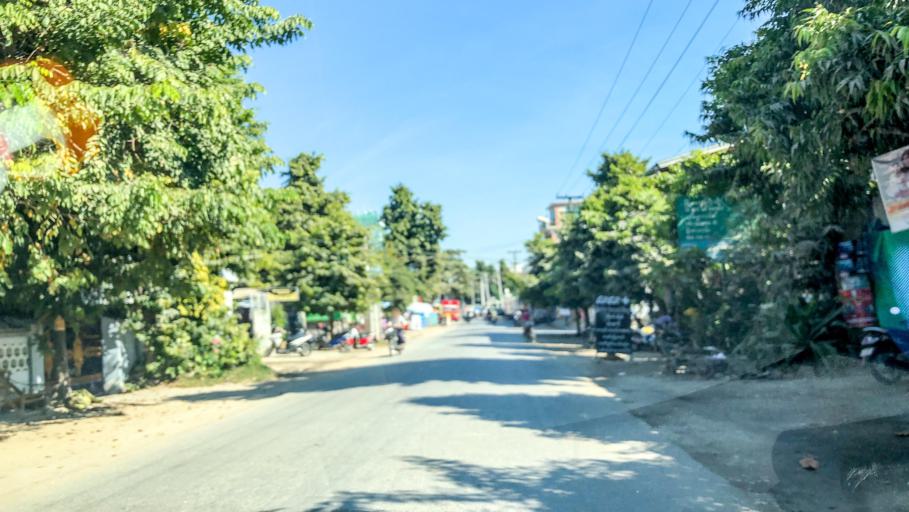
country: MM
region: Sagain
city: Sagaing
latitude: 21.8793
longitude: 95.9785
